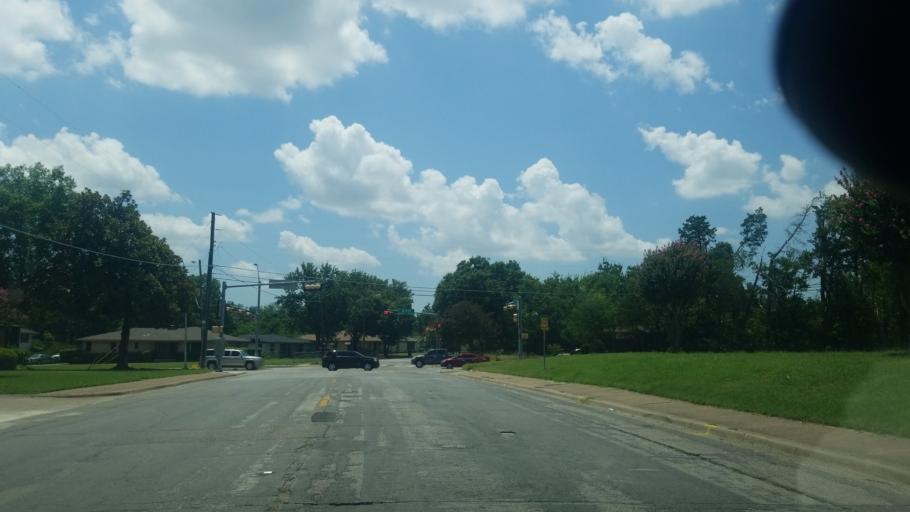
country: US
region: Texas
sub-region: Dallas County
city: Dallas
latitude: 32.7204
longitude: -96.7828
